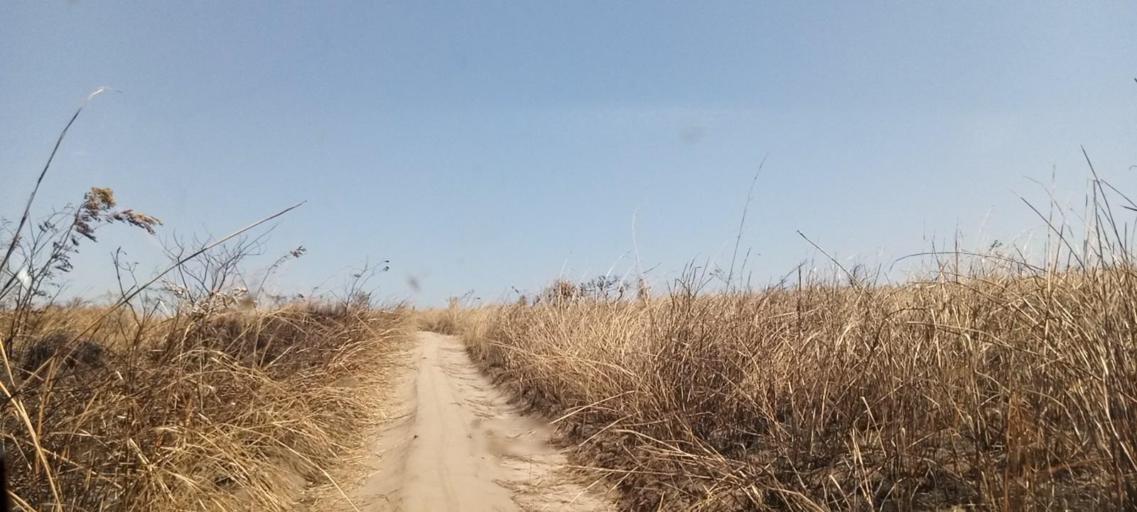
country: CD
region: Kasai-Oriental
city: Kabinda
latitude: -5.9419
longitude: 24.8065
